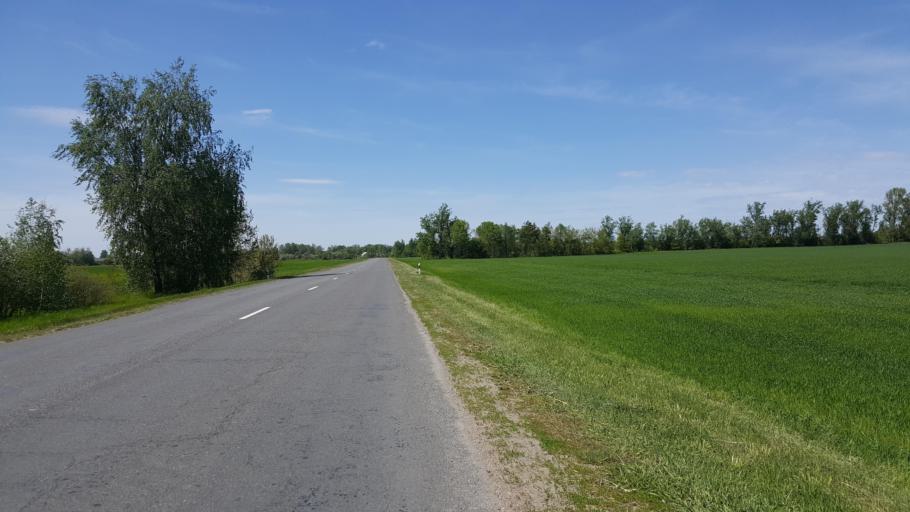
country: BY
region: Brest
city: Kobryn
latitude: 52.3485
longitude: 24.1981
